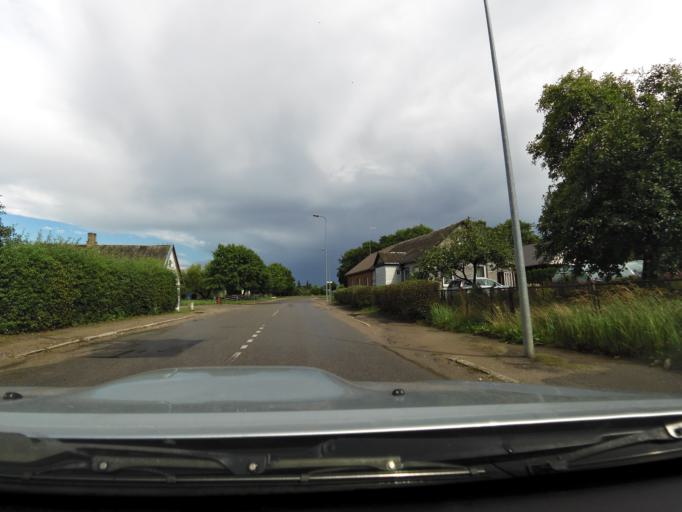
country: LT
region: Vilnius County
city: Ukmerge
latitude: 55.2540
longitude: 24.7527
